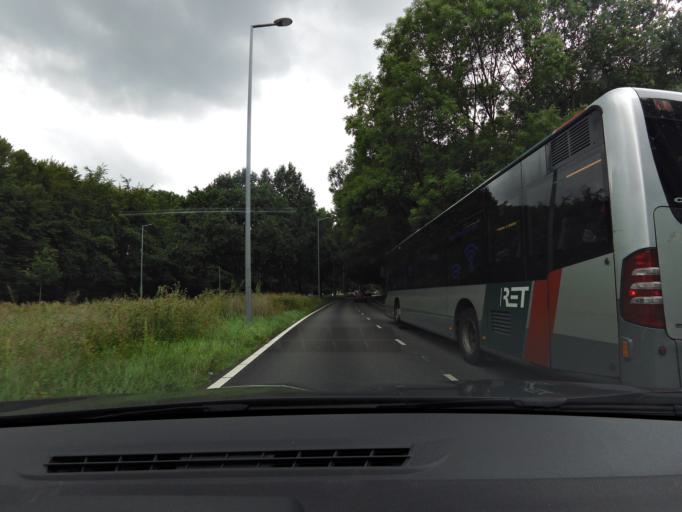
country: NL
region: South Holland
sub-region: Gemeente Rotterdam
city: Delfshaven
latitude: 51.8814
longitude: 4.4696
